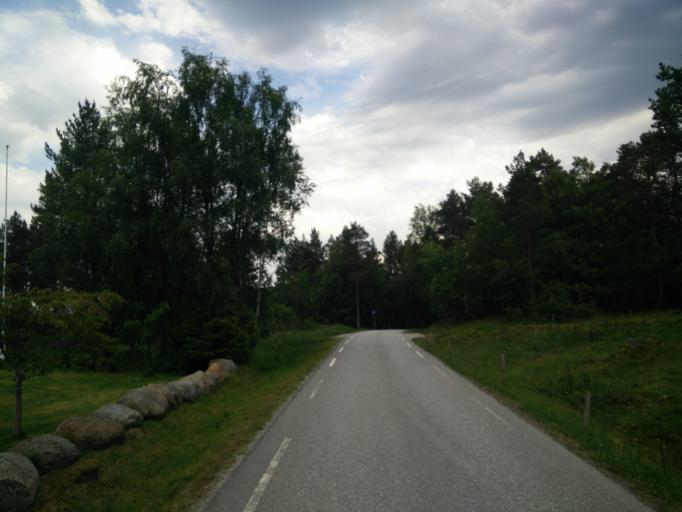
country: NO
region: More og Romsdal
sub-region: Kristiansund
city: Rensvik
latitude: 63.0349
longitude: 7.9552
